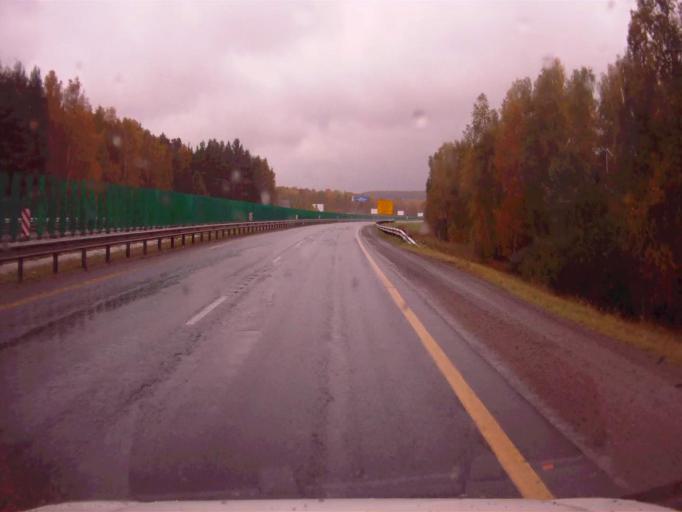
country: RU
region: Chelyabinsk
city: Dolgoderevenskoye
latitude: 55.3389
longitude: 61.3074
